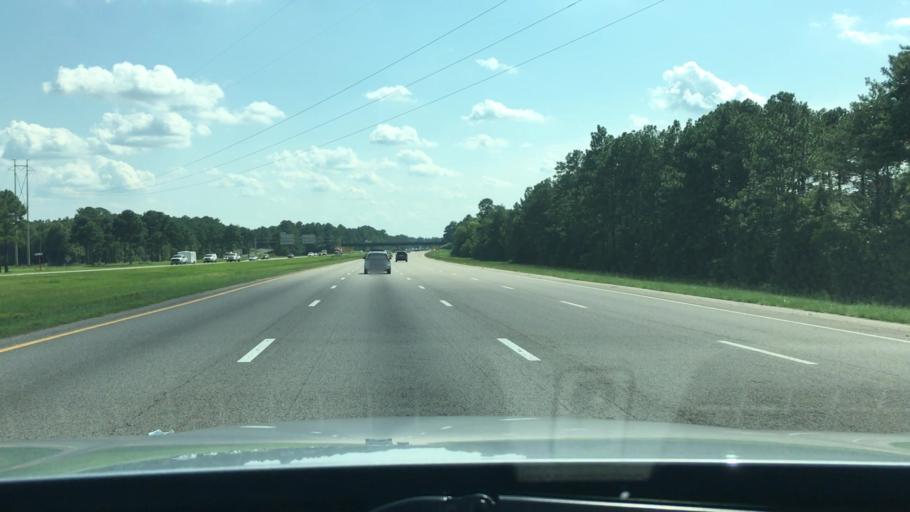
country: US
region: North Carolina
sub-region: Cumberland County
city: Hope Mills
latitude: 34.9269
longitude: -78.9420
